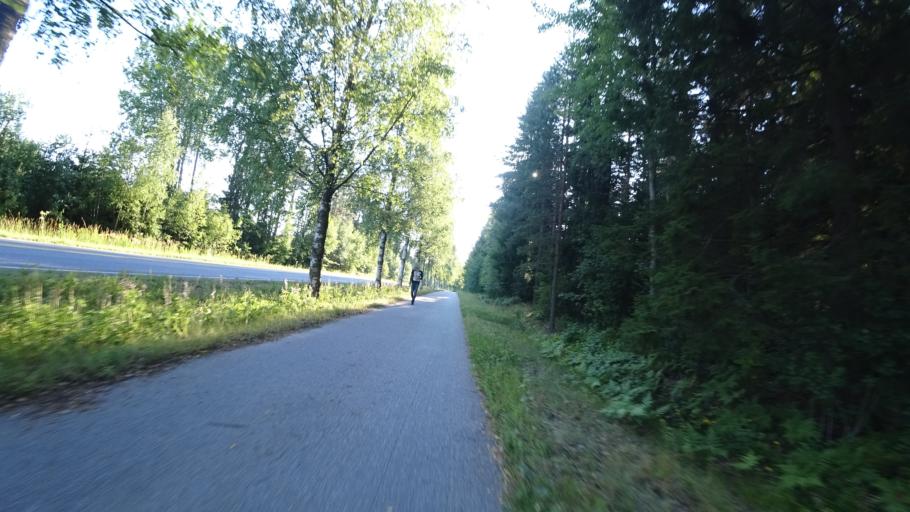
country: FI
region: Pirkanmaa
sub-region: Tampere
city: Nokia
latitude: 61.4664
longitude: 23.4312
